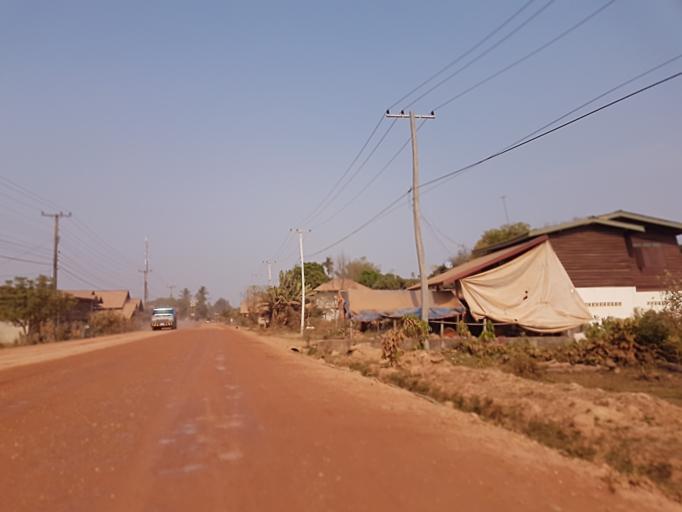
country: TH
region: Nong Khai
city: Nong Khai
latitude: 17.9379
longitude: 102.7875
